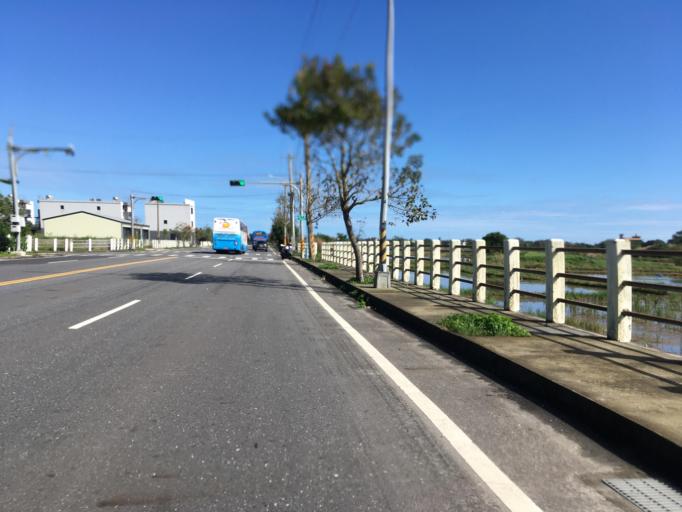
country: TW
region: Taiwan
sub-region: Yilan
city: Yilan
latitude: 24.6148
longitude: 121.8439
